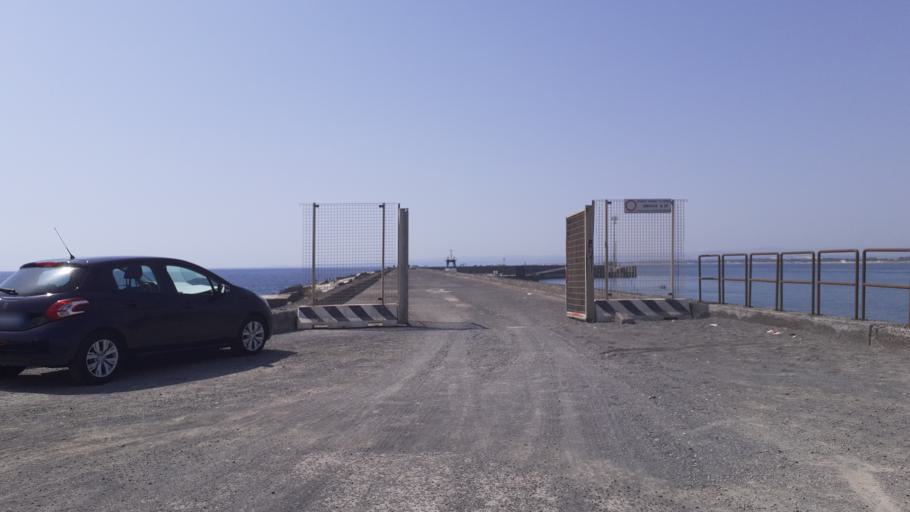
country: IT
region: Sicily
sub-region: Catania
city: Catania
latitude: 37.4911
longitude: 15.0999
